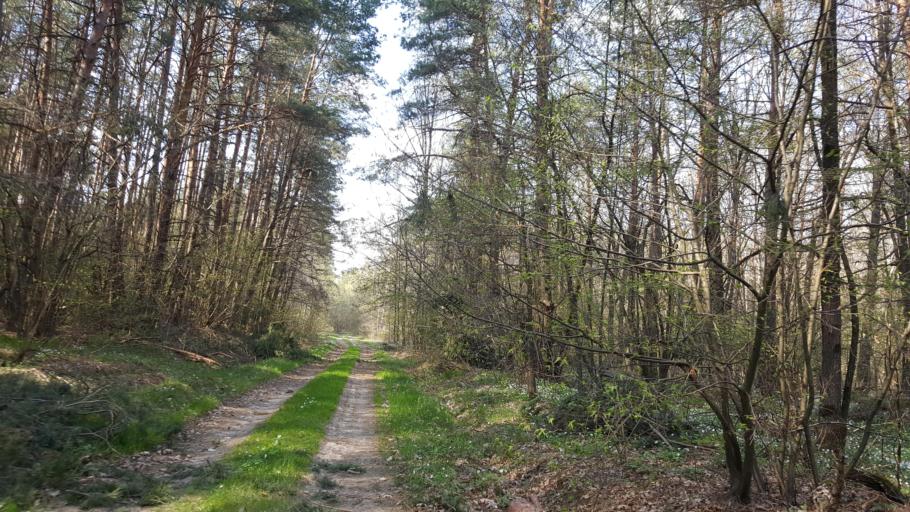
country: BY
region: Brest
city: Kamyanyets
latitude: 52.3348
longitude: 23.8513
